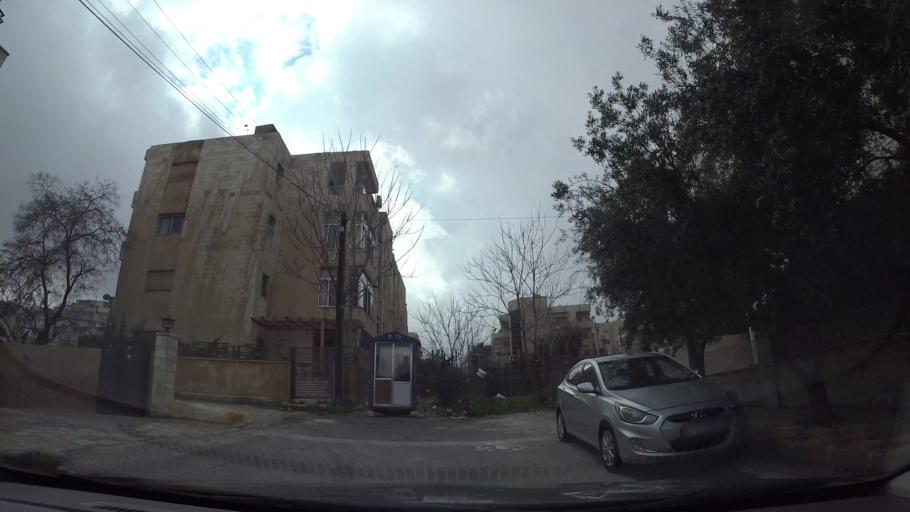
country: JO
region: Amman
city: Wadi as Sir
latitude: 31.9506
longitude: 35.8756
